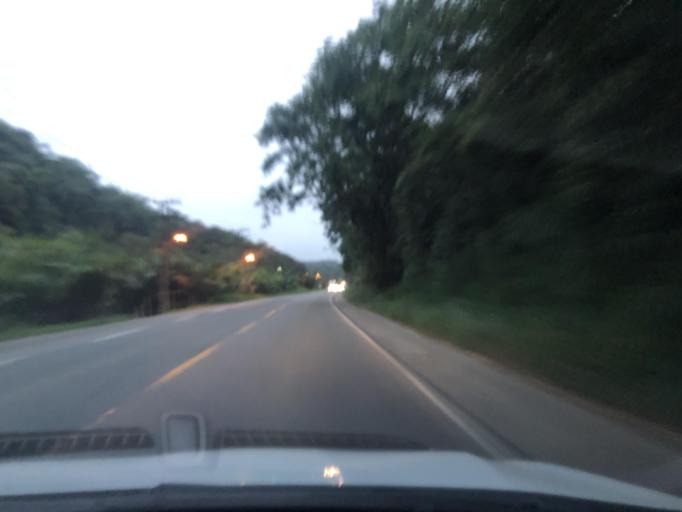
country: BR
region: Santa Catarina
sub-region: Pomerode
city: Pomerode
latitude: -26.7079
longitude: -49.0548
